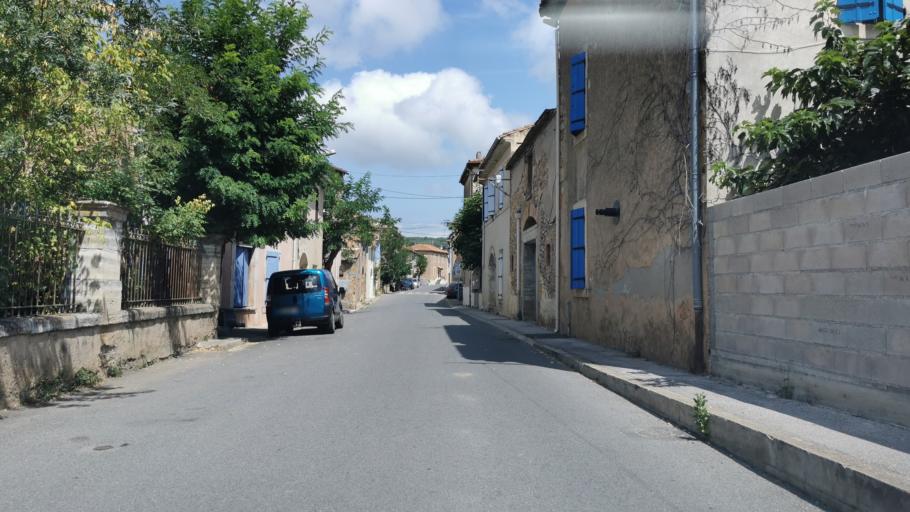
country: FR
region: Languedoc-Roussillon
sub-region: Departement de l'Aude
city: Bizanet
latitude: 43.1652
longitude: 2.8714
